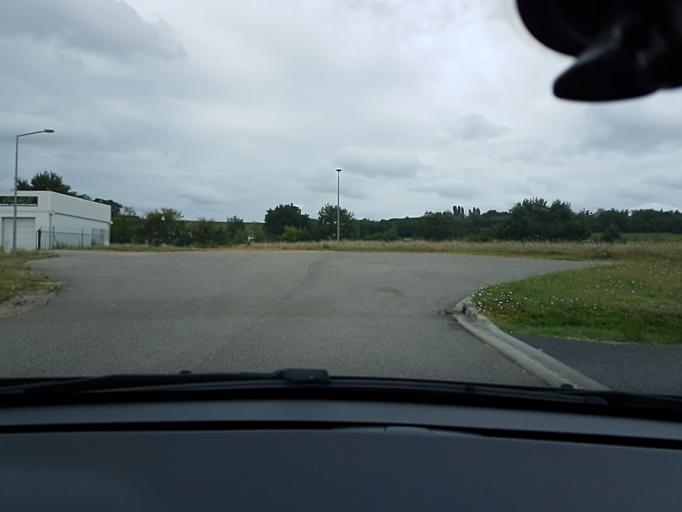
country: FR
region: Aquitaine
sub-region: Departement du Lot-et-Garonne
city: Nerac
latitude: 44.1504
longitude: 0.3210
